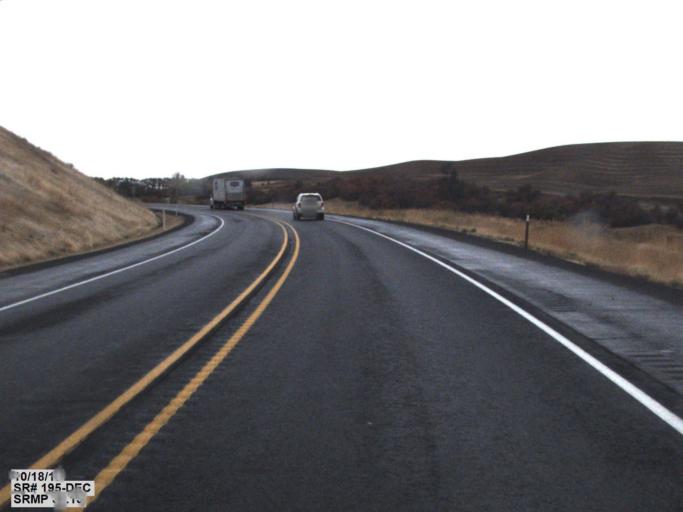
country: US
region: Washington
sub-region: Whitman County
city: Colfax
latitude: 46.8379
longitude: -117.3382
